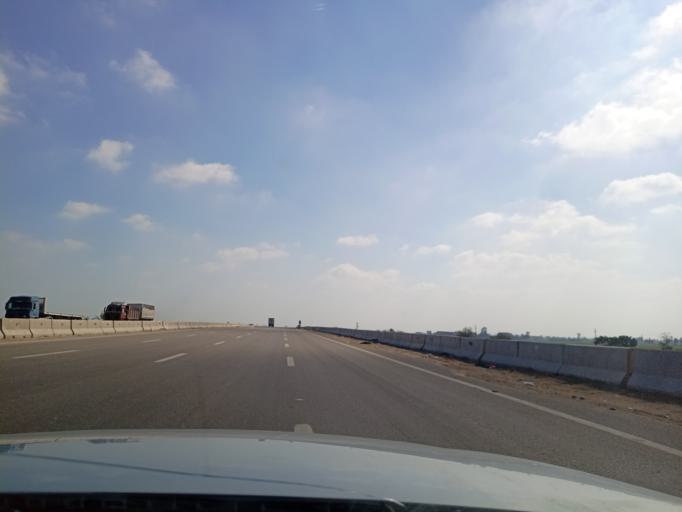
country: EG
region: Eastern Province
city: Mashtul as Suq
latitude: 30.4537
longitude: 31.4027
